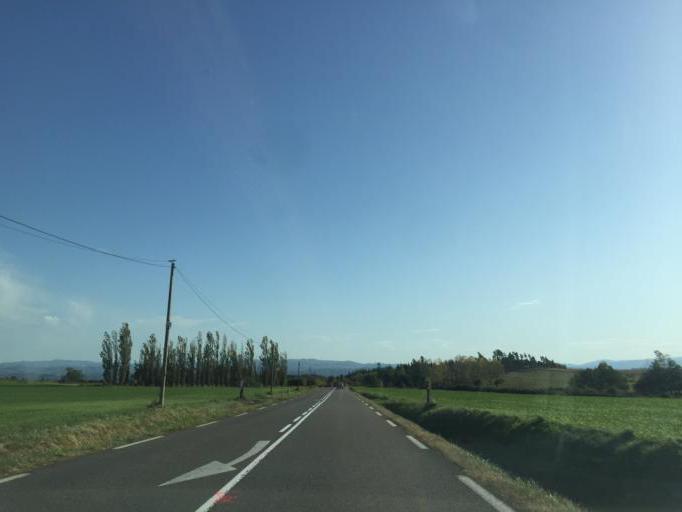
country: FR
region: Rhone-Alpes
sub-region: Departement de la Loire
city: Perigneux
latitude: 45.4698
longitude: 4.1338
